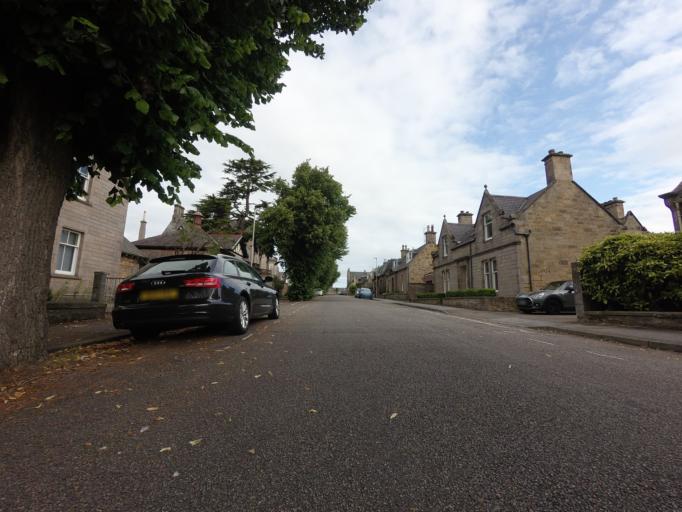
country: GB
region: Scotland
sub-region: Moray
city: Elgin
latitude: 57.6454
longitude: -3.3129
